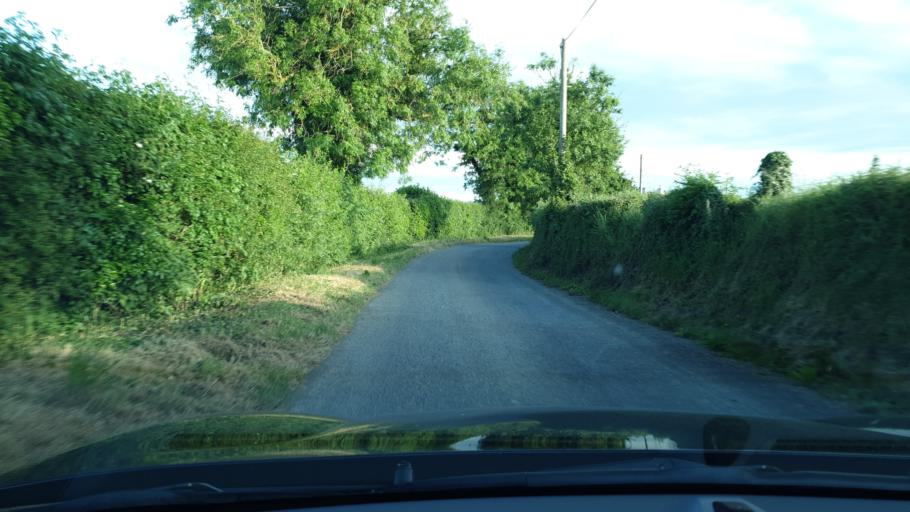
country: IE
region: Leinster
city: Hartstown
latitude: 53.4348
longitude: -6.4039
